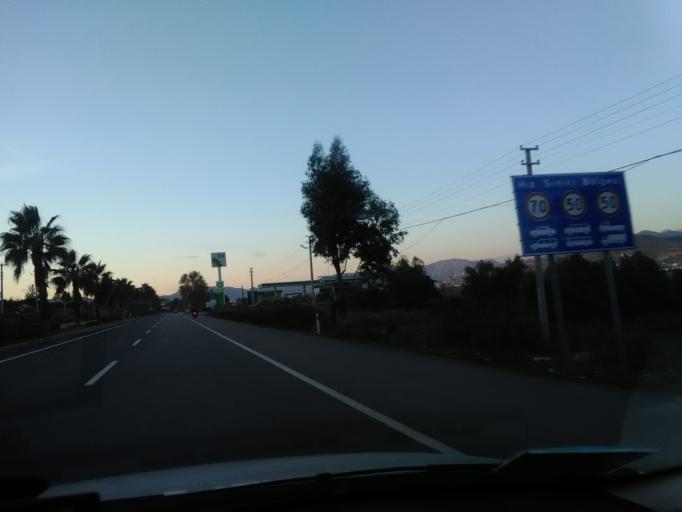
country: TR
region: Antalya
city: Gazipasa
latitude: 36.2510
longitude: 32.3390
